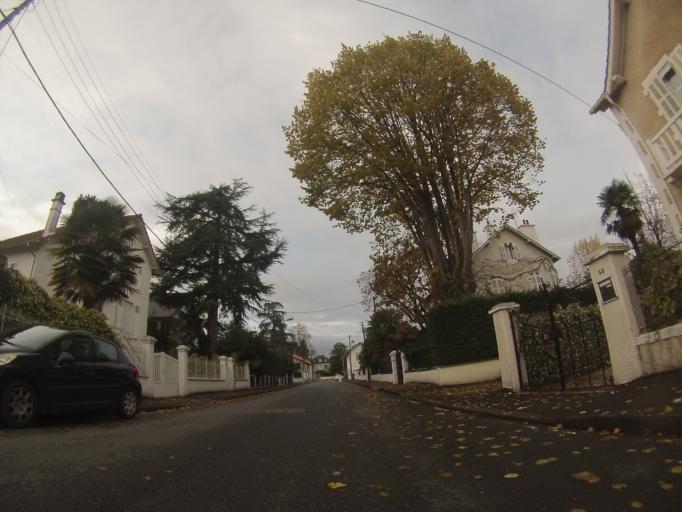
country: FR
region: Aquitaine
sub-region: Departement des Pyrenees-Atlantiques
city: Jurancon
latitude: 43.2842
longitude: -0.3832
